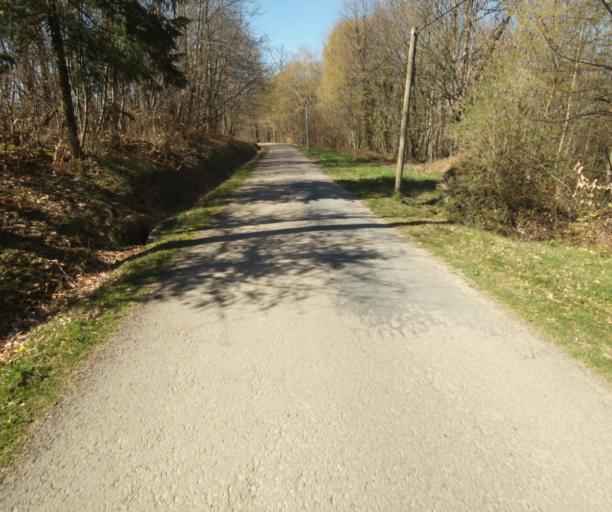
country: FR
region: Limousin
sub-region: Departement de la Correze
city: Chameyrat
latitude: 45.2518
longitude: 1.7104
